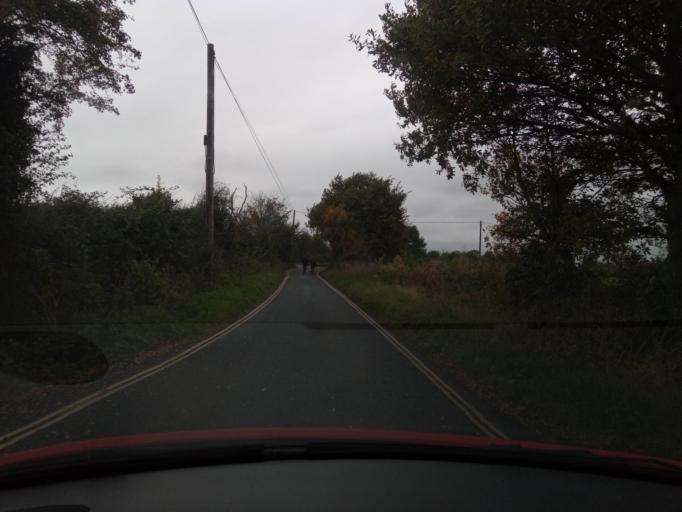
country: GB
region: England
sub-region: Essex
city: Brightlingsea
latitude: 51.7938
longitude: 0.9862
